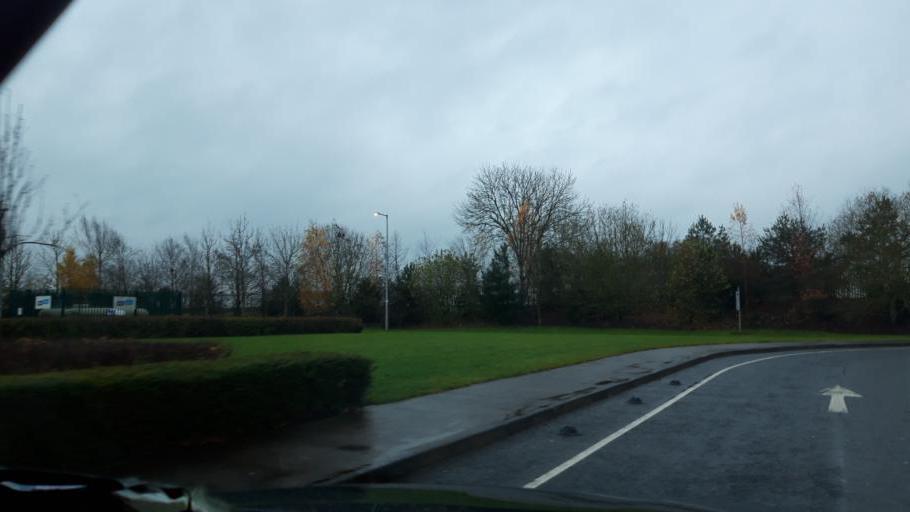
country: IE
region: Leinster
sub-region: An Mhi
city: Enfield
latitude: 53.4111
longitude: -6.8772
